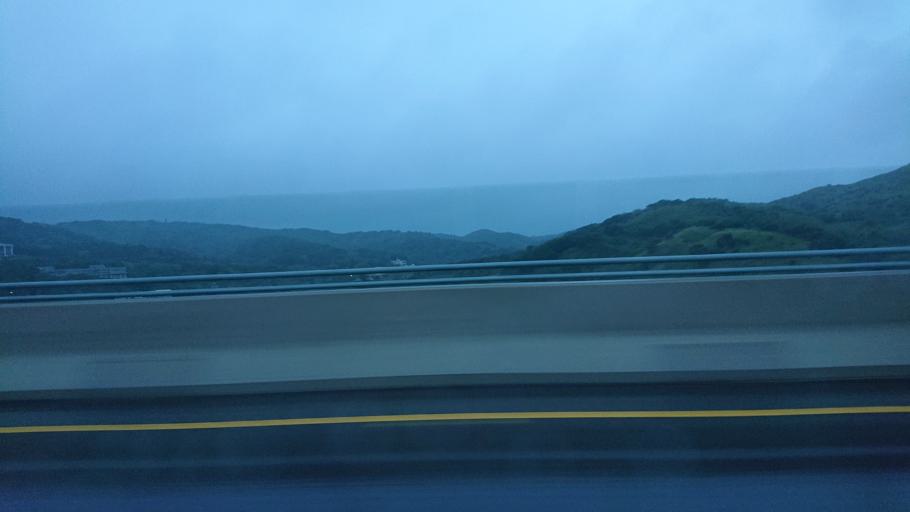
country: TW
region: Taiwan
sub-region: Miaoli
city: Miaoli
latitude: 24.5547
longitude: 120.7099
